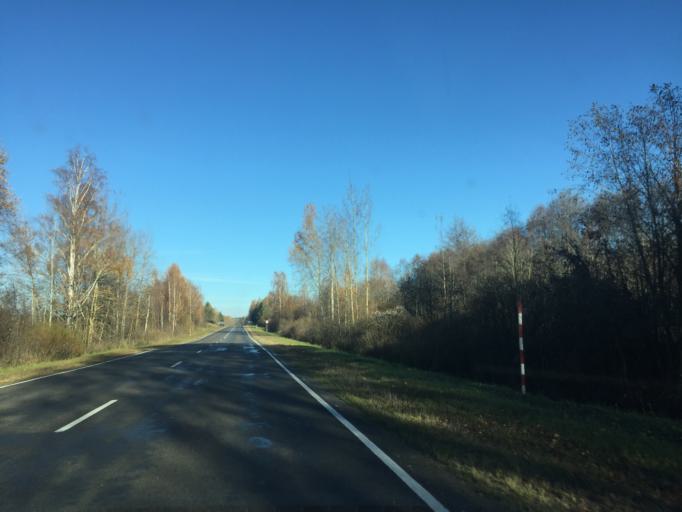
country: BY
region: Vitebsk
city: Dzisna
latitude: 55.3598
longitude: 28.3469
